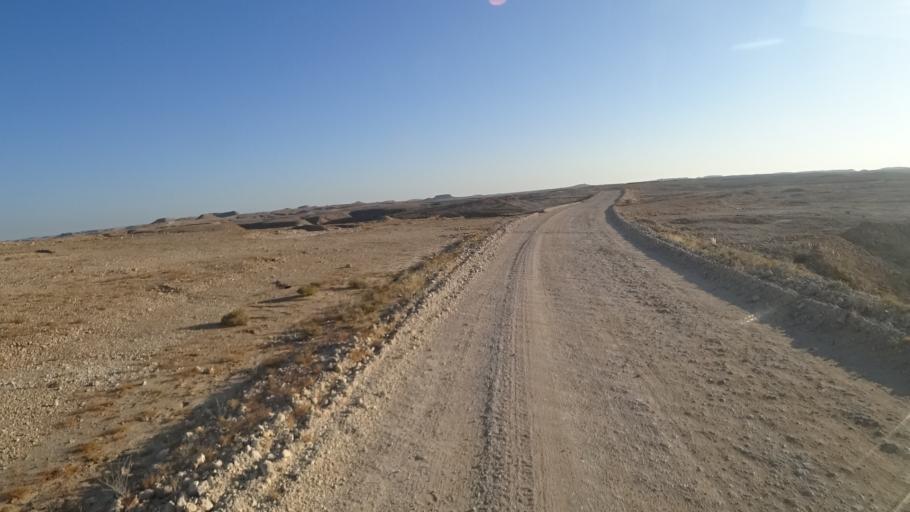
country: YE
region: Al Mahrah
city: Hawf
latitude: 17.1638
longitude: 53.3516
